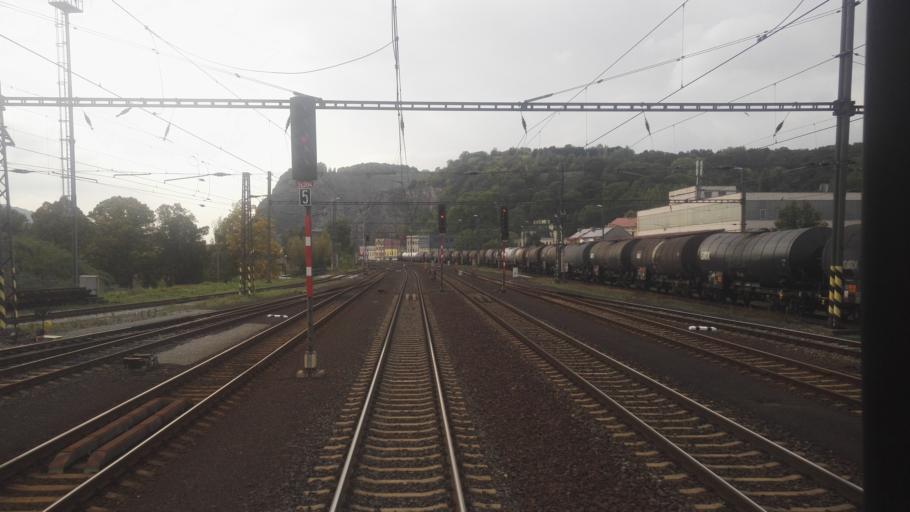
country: CZ
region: Ustecky
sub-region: Okres Usti nad Labem
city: Usti nad Labem
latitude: 50.6636
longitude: 14.0662
